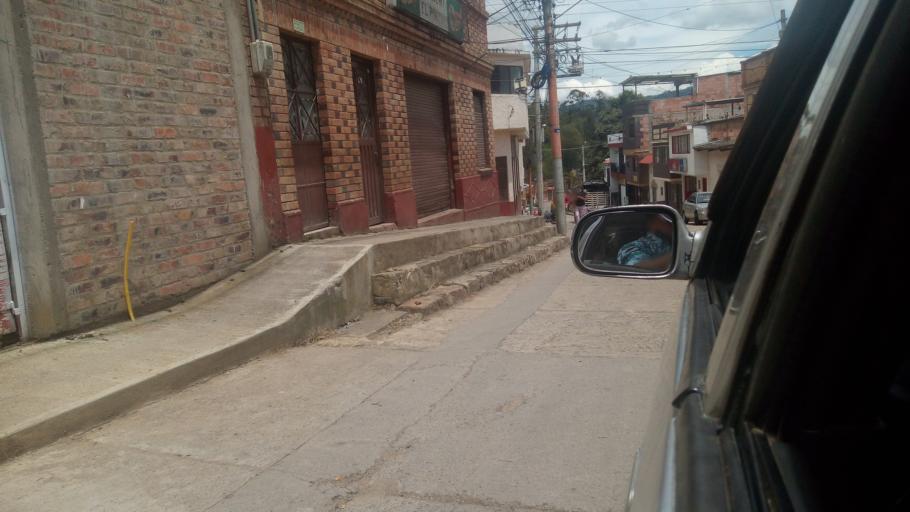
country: CO
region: Cundinamarca
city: Manta
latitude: 5.0094
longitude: -73.5408
